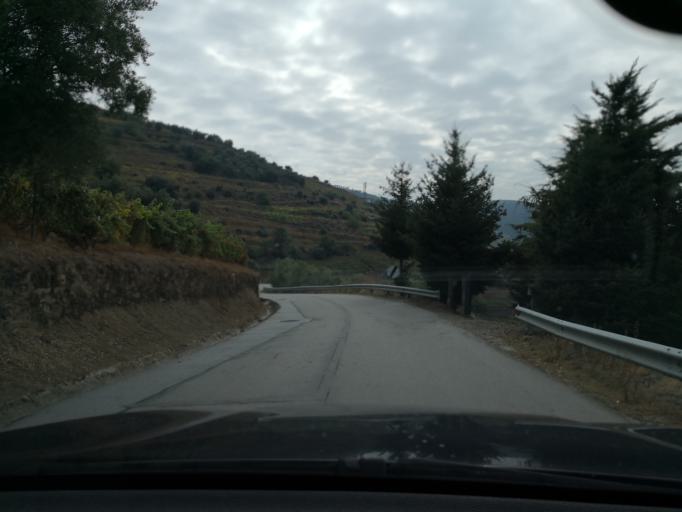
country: PT
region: Vila Real
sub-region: Peso da Regua
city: Peso da Regua
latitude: 41.1840
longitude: -7.7415
